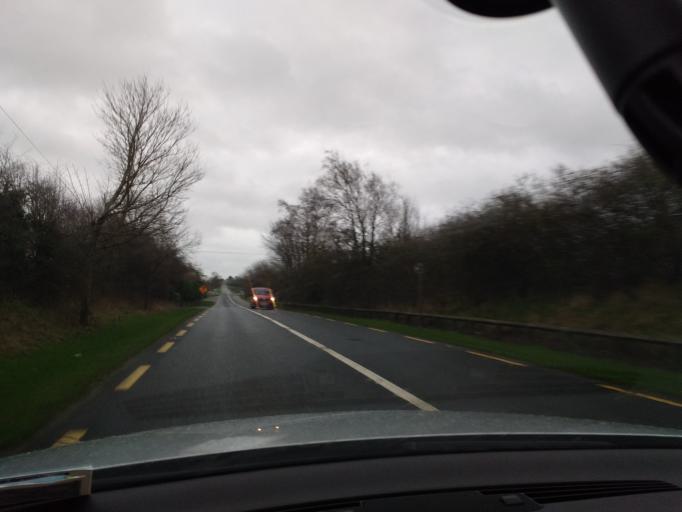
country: IE
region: Munster
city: Thurles
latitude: 52.6768
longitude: -7.7836
